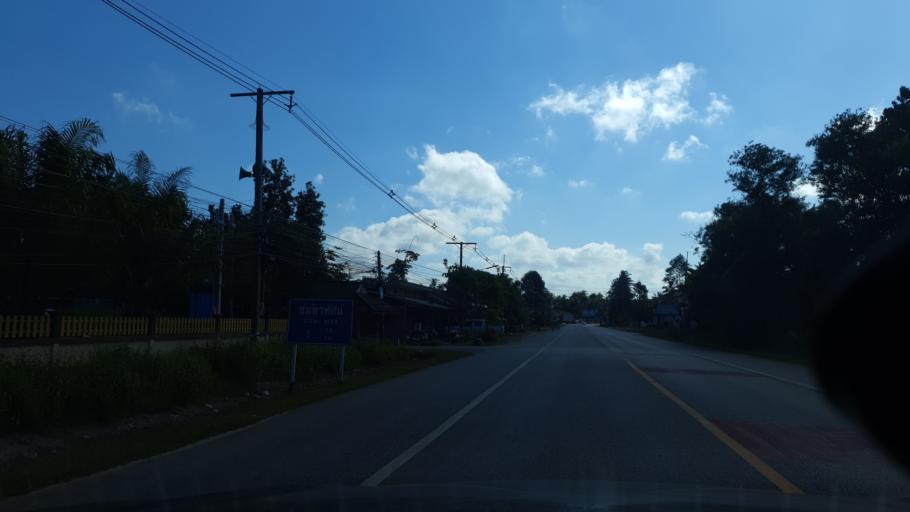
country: TH
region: Krabi
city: Krabi
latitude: 8.0264
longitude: 98.8794
